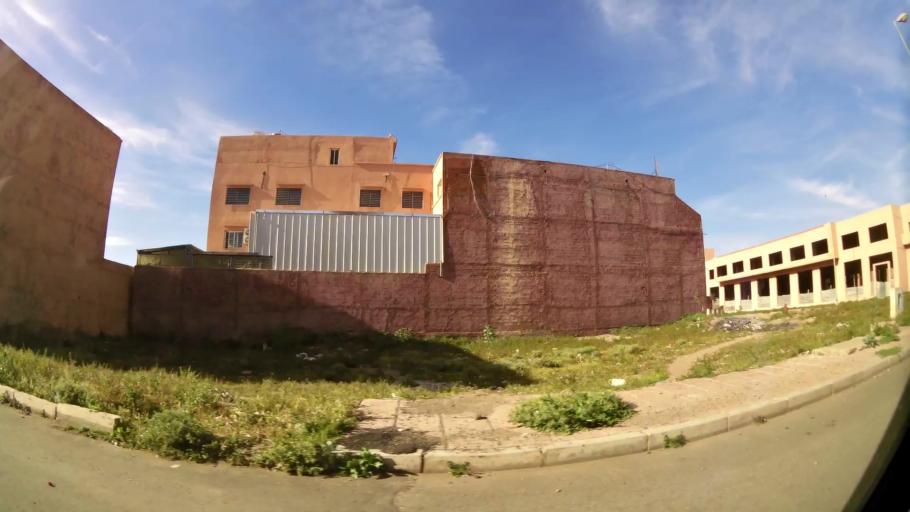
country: MA
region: Marrakech-Tensift-Al Haouz
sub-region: Marrakech
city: Marrakesh
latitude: 31.6780
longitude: -8.0379
